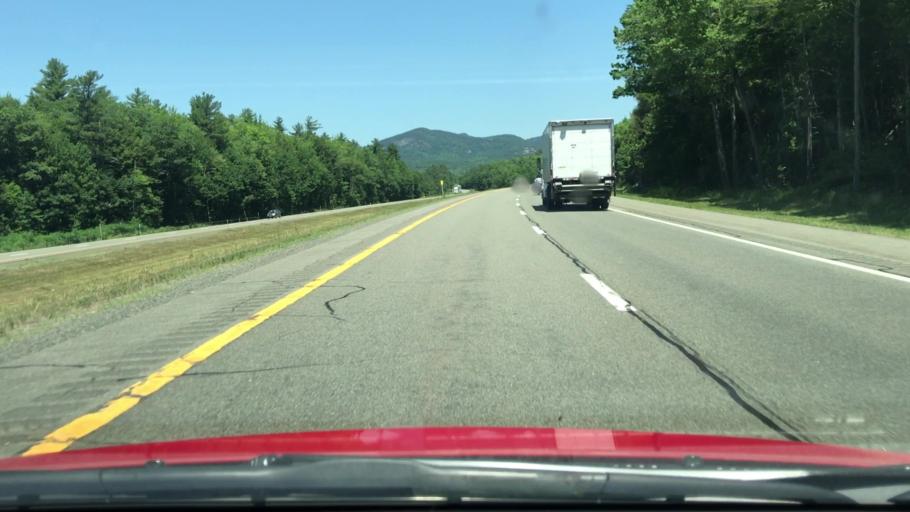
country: US
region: New York
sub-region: Essex County
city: Elizabethtown
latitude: 44.3362
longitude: -73.5334
